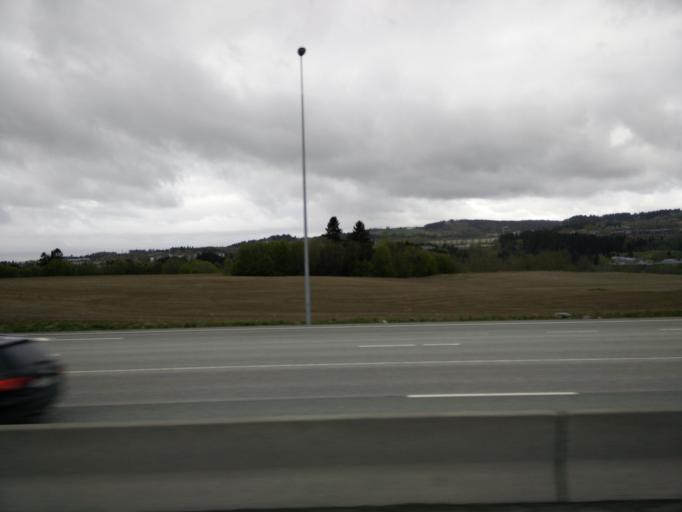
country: NO
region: Sor-Trondelag
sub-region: Trondheim
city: Trondheim
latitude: 63.3732
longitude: 10.3788
